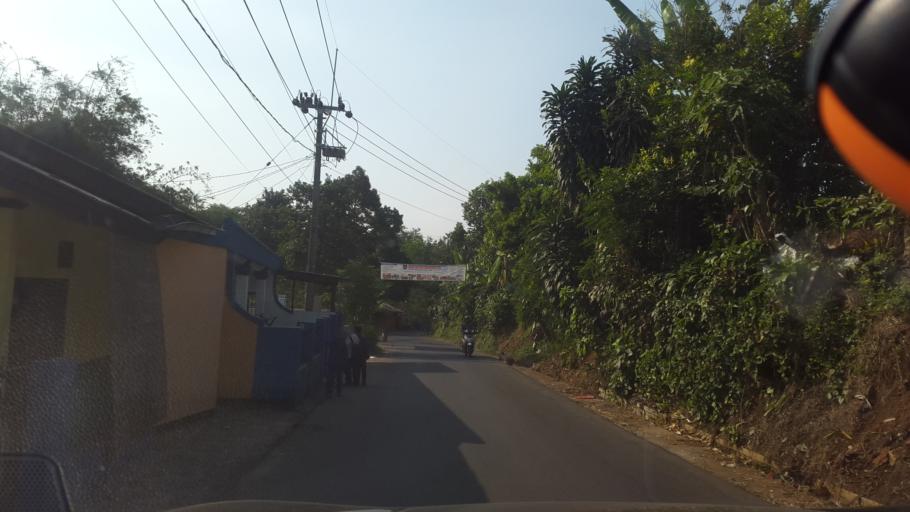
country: ID
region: West Java
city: Sukabumi
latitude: -6.8846
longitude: 106.8294
